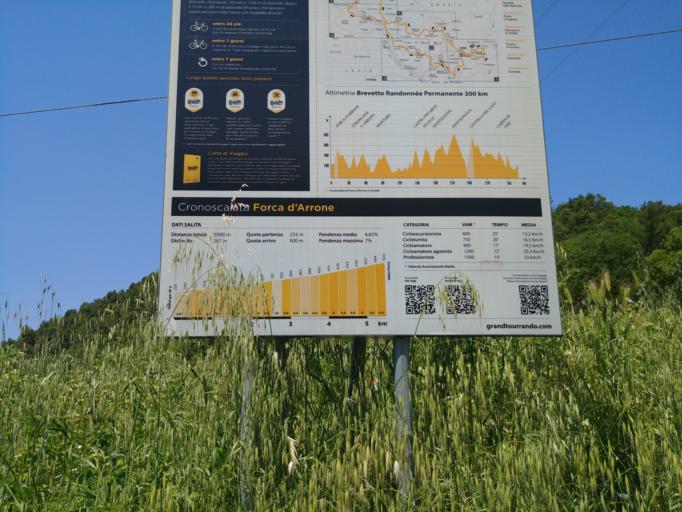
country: IT
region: Umbria
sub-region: Provincia di Terni
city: Arrone
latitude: 42.5600
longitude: 12.7762
